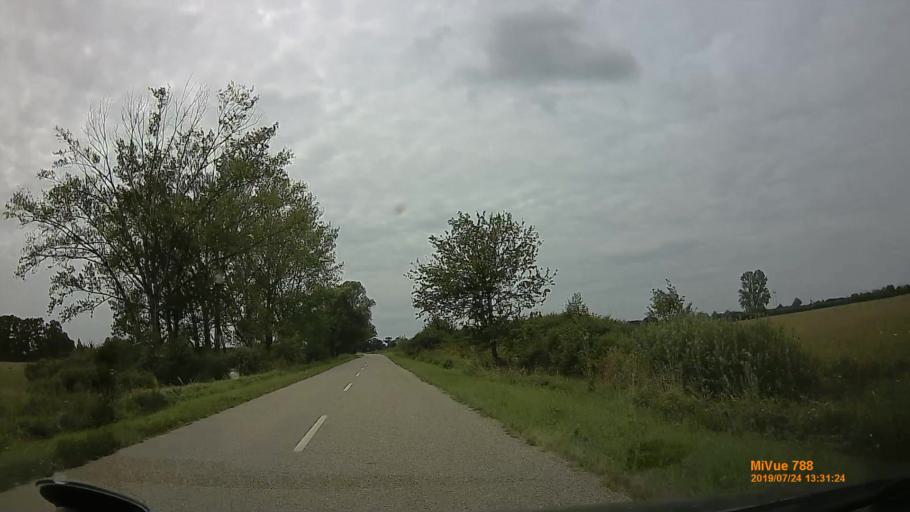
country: HU
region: Szabolcs-Szatmar-Bereg
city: Aranyosapati
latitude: 48.2315
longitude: 22.3603
